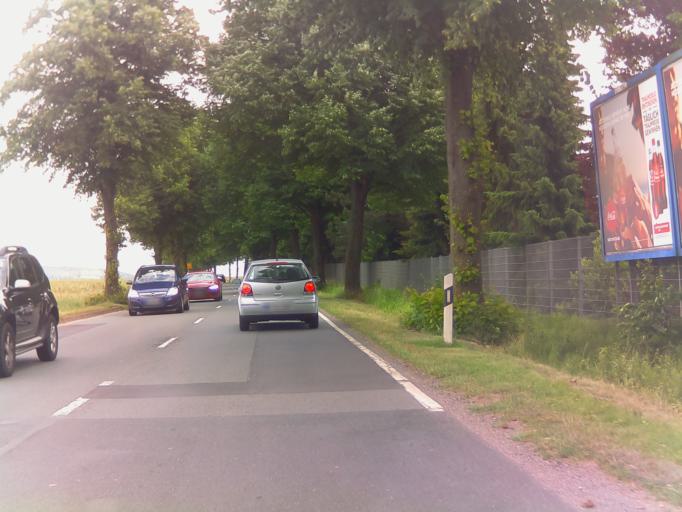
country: DE
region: Lower Saxony
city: Elze
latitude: 52.1712
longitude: 9.6721
